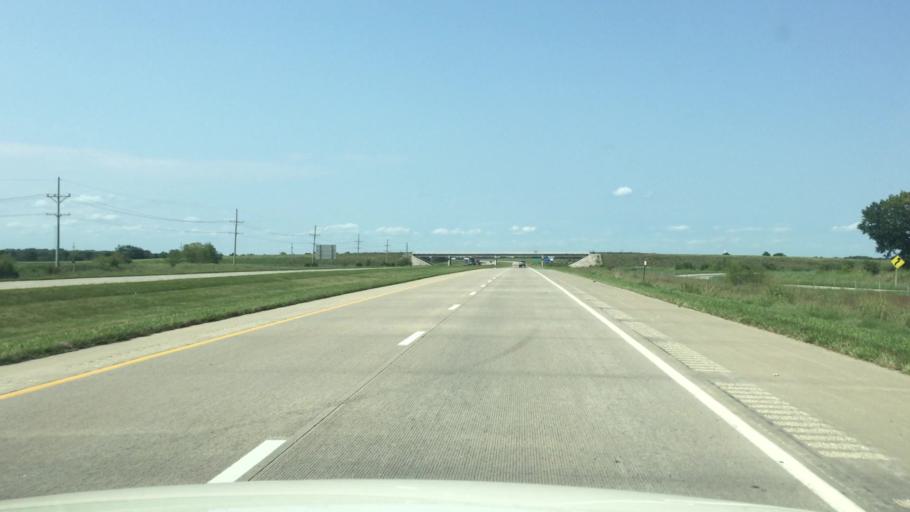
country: US
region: Kansas
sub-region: Linn County
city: Pleasanton
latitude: 38.1631
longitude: -94.6957
